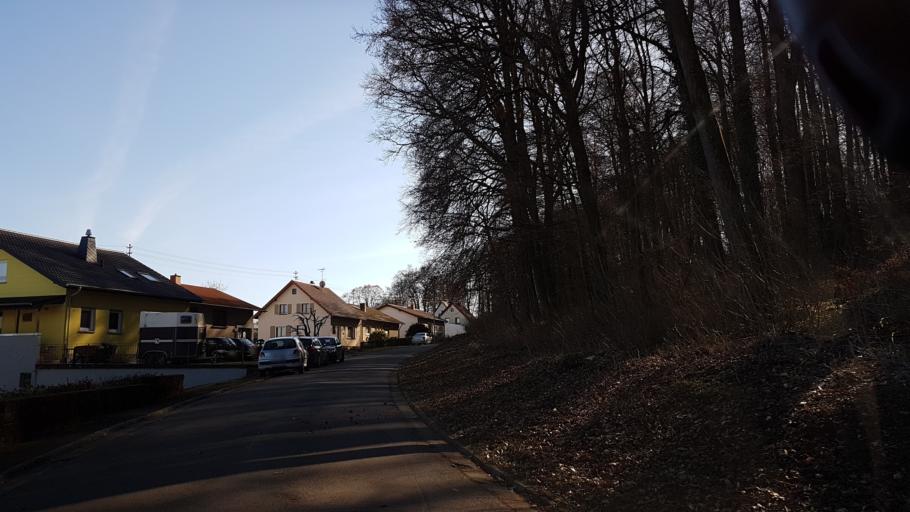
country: DE
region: Saarland
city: Oberthal
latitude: 49.4744
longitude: 7.0962
